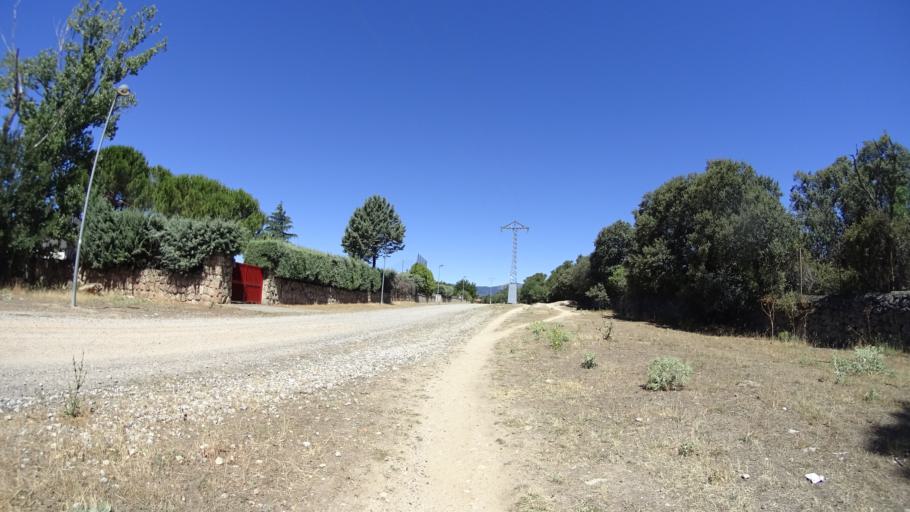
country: ES
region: Madrid
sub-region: Provincia de Madrid
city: Alpedrete
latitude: 40.6471
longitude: -4.0367
